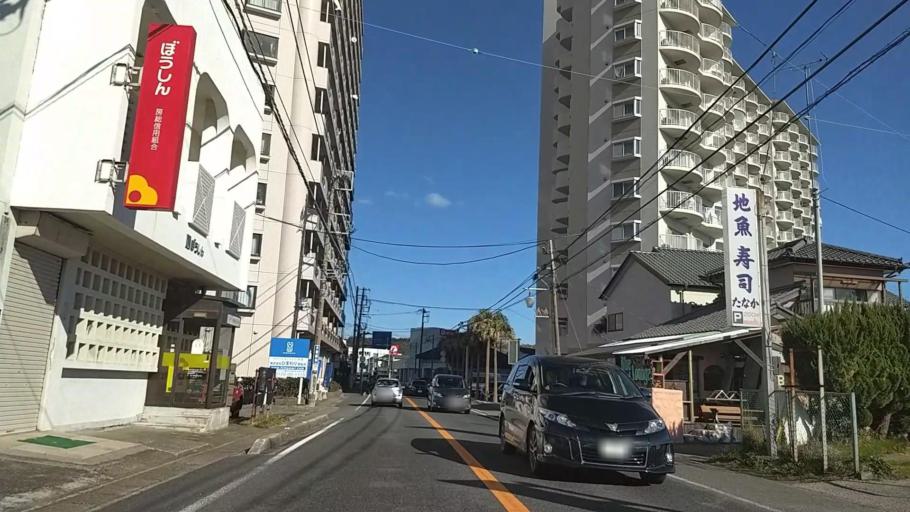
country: JP
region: Chiba
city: Katsuura
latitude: 35.1856
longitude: 140.3532
